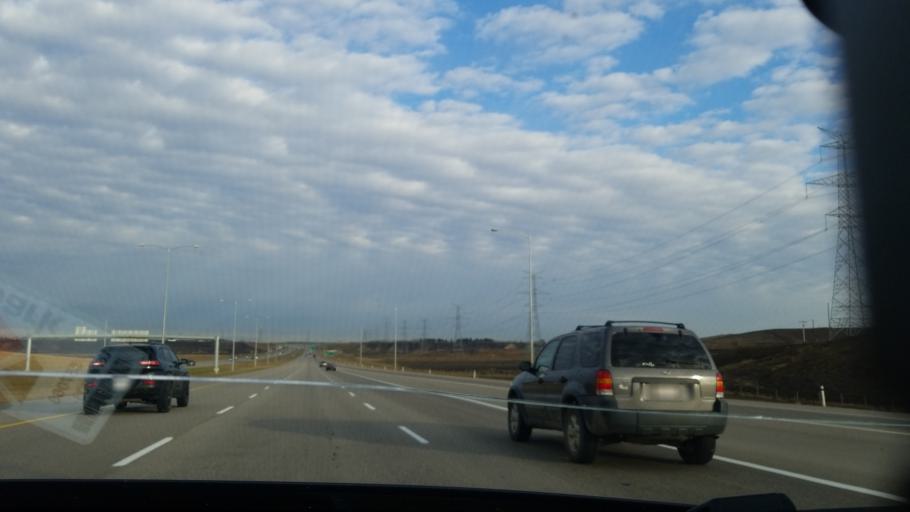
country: CA
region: Alberta
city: Sherwood Park
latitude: 53.5927
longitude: -113.3469
